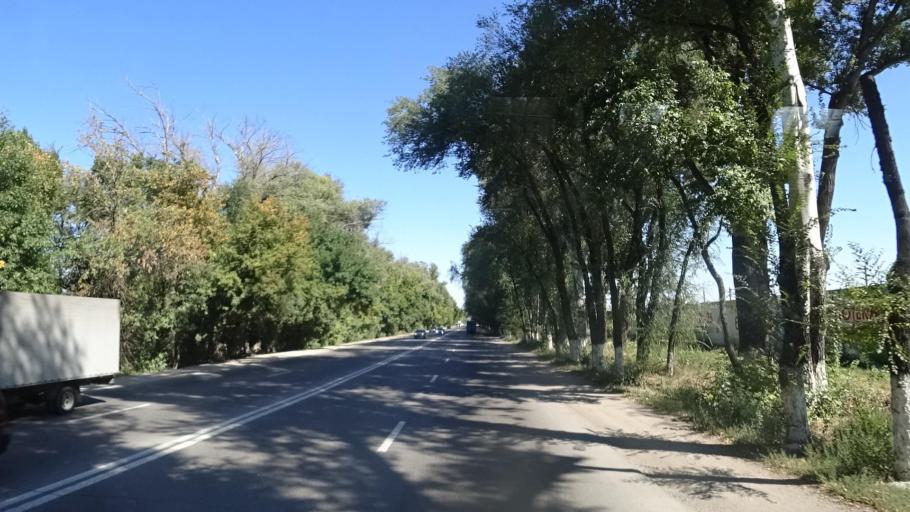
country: KZ
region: Almaty Oblysy
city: Pervomayskiy
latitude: 43.3239
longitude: 77.0292
